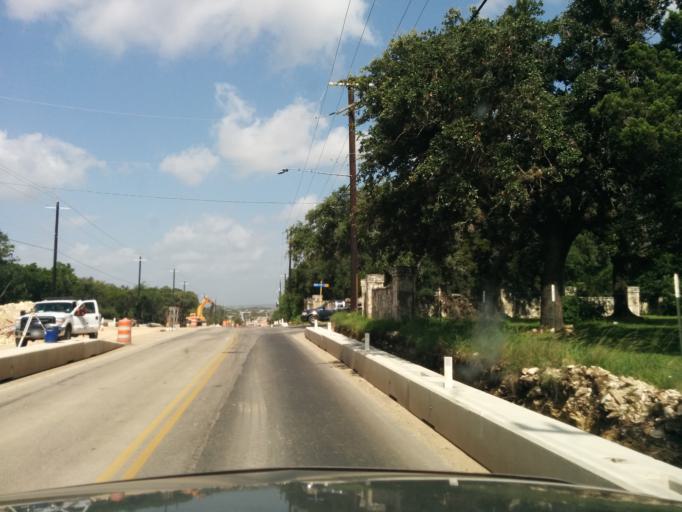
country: US
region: Texas
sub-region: Bexar County
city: Helotes
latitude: 29.5723
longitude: -98.6241
